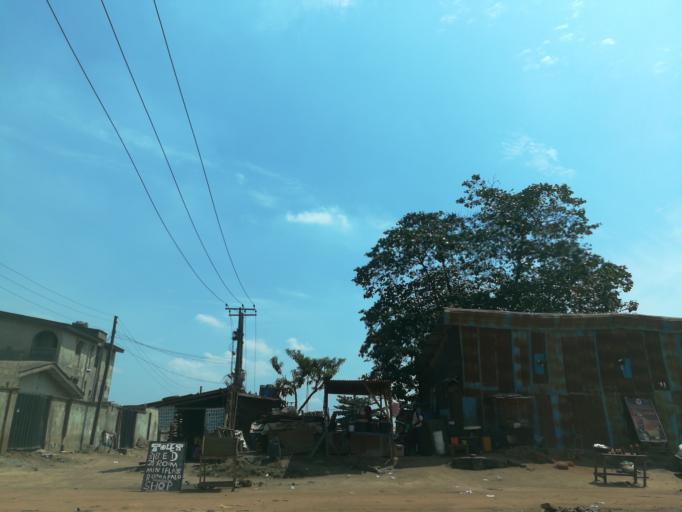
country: NG
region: Lagos
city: Ikorodu
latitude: 6.6574
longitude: 3.4756
